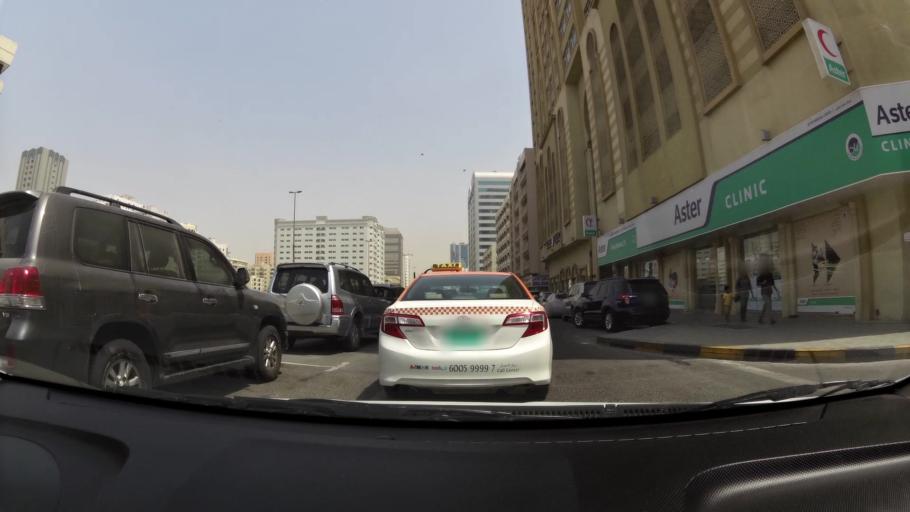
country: AE
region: Ash Shariqah
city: Sharjah
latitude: 25.3378
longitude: 55.3892
